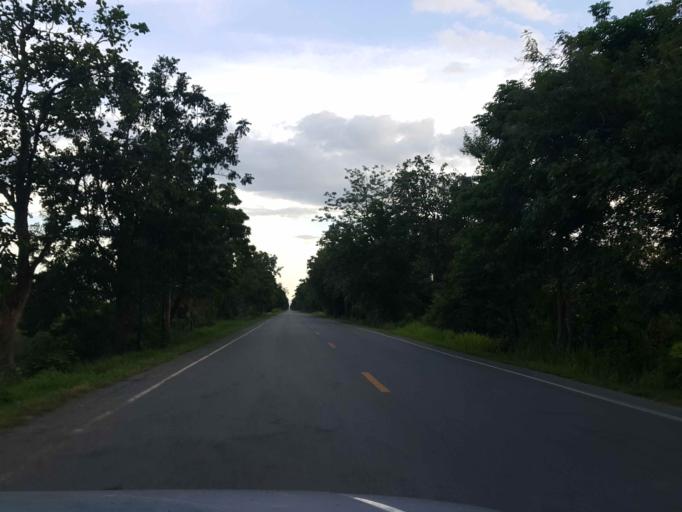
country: TH
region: Sukhothai
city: Sawankhalok
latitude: 17.3259
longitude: 99.7381
